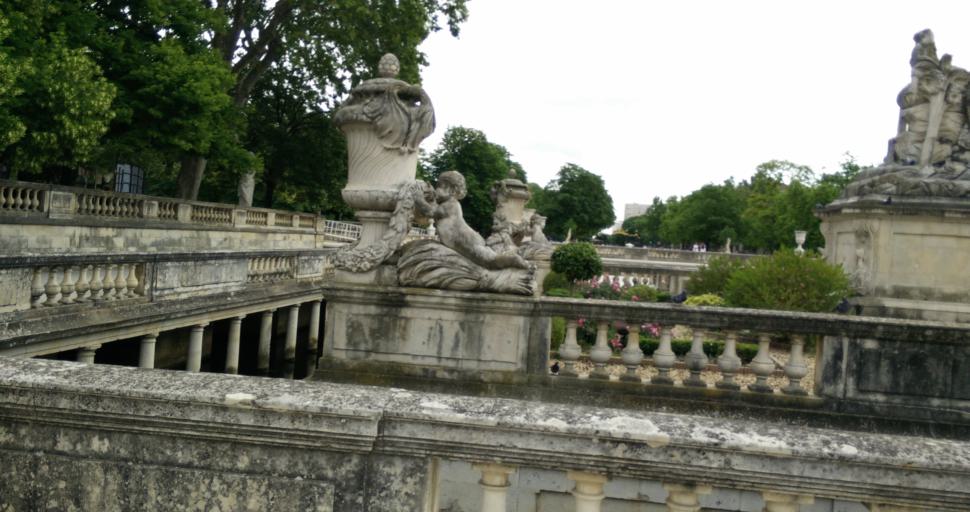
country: FR
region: Languedoc-Roussillon
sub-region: Departement du Gard
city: Nimes
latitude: 43.8401
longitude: 4.3495
